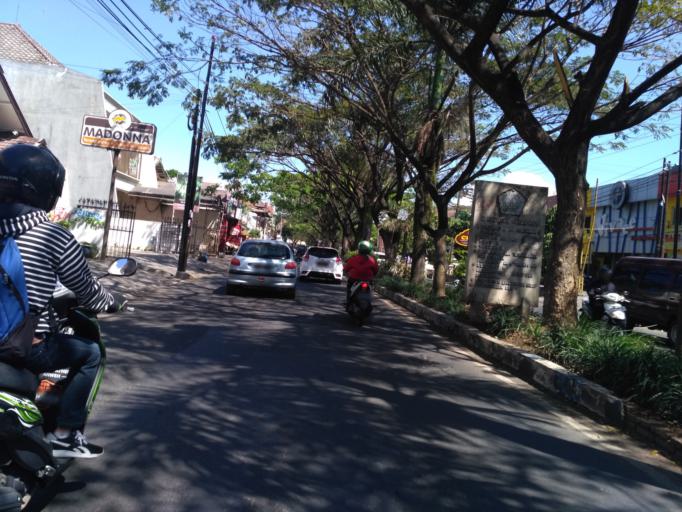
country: ID
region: East Java
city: Malang
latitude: -7.9804
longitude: 112.6571
